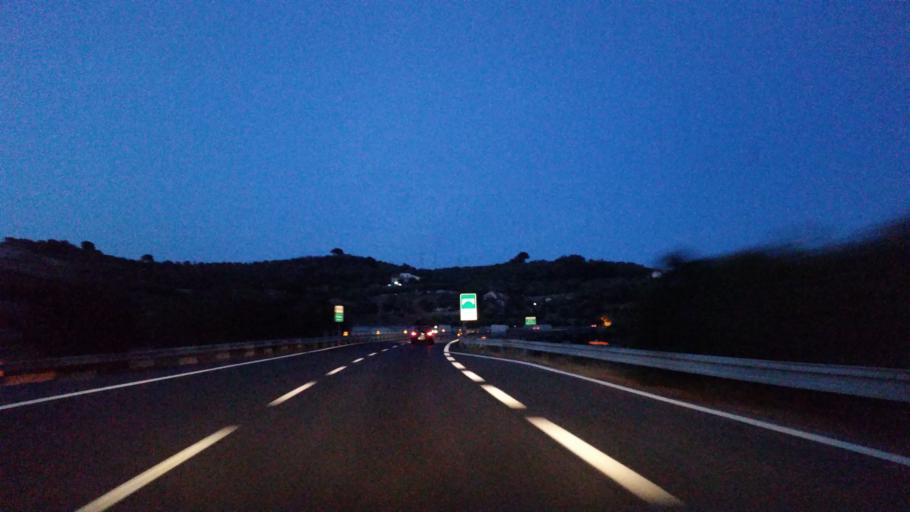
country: IT
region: Liguria
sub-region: Provincia di Imperia
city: Diano Castello
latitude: 43.9215
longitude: 8.0733
